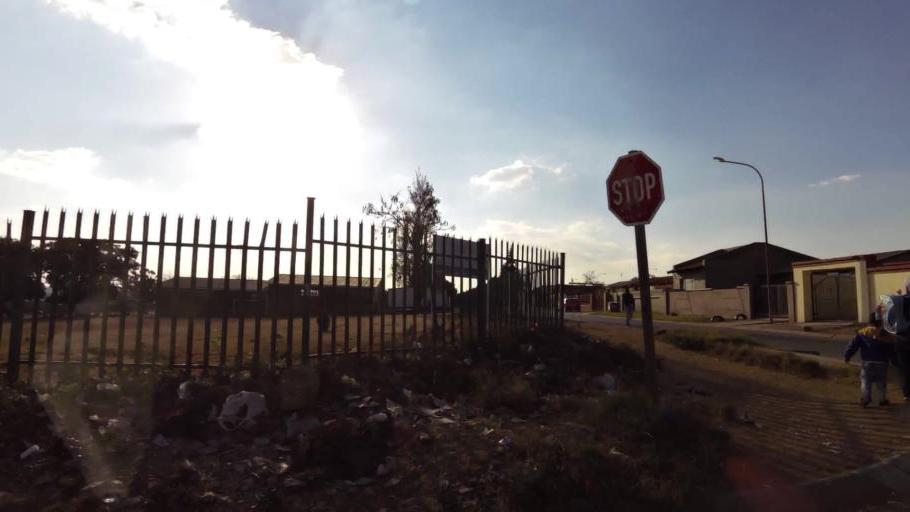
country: ZA
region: Gauteng
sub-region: City of Johannesburg Metropolitan Municipality
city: Soweto
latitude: -26.2273
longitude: 27.8931
